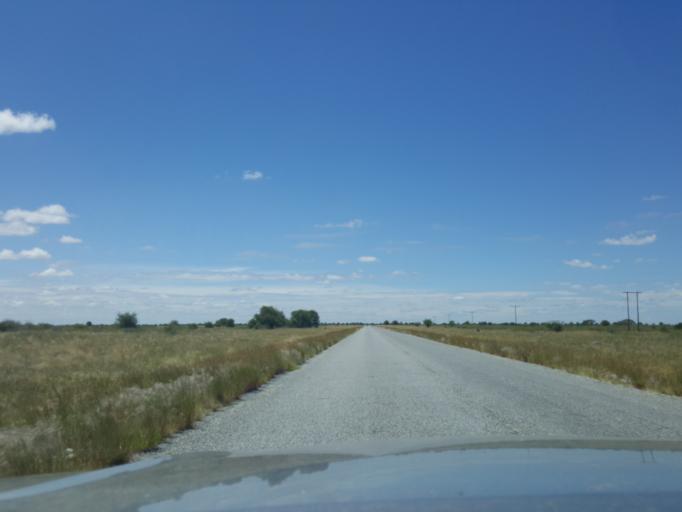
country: BW
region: Central
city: Nata
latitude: -20.1997
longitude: 26.1144
